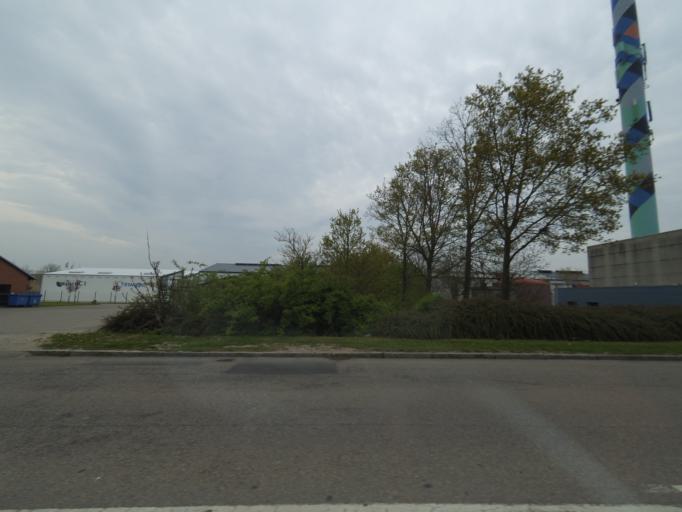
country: DK
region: South Denmark
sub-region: Odense Kommune
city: Bellinge
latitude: 55.3545
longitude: 10.3350
